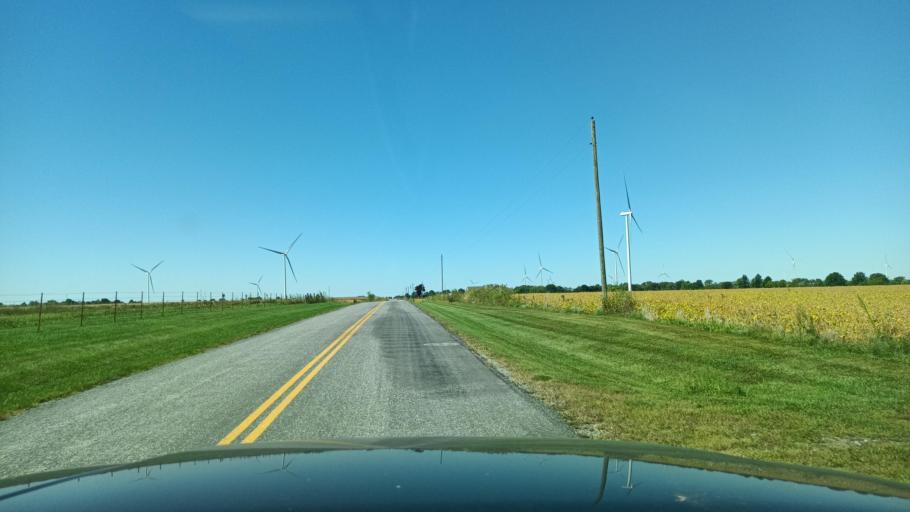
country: US
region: Missouri
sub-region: Adair County
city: Kirksville
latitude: 40.3307
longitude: -92.4732
